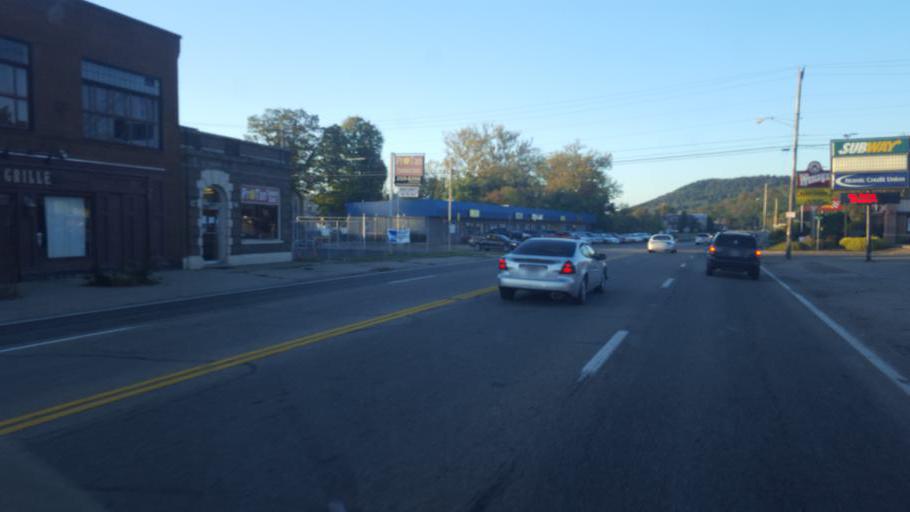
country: US
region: Ohio
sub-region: Scioto County
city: Lucasville
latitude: 38.8800
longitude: -82.9968
